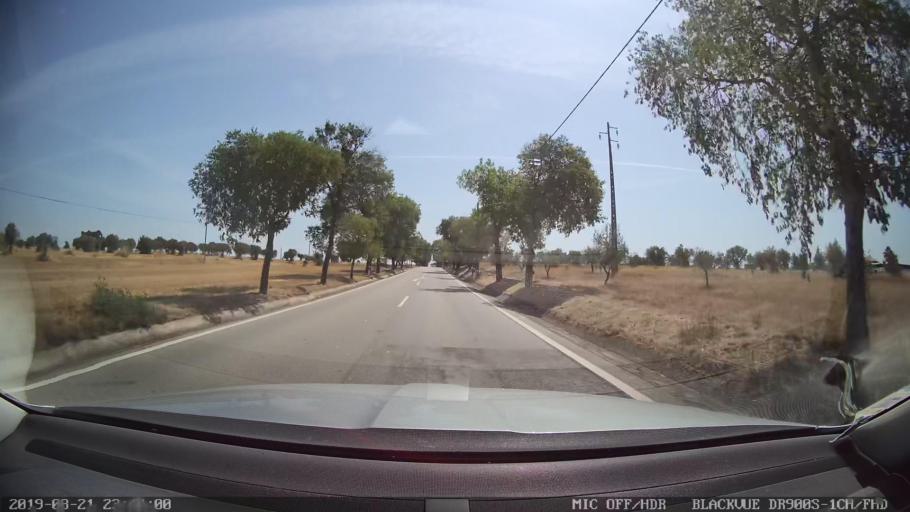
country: PT
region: Castelo Branco
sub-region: Idanha-A-Nova
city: Idanha-a-Nova
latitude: 39.8479
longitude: -7.2860
